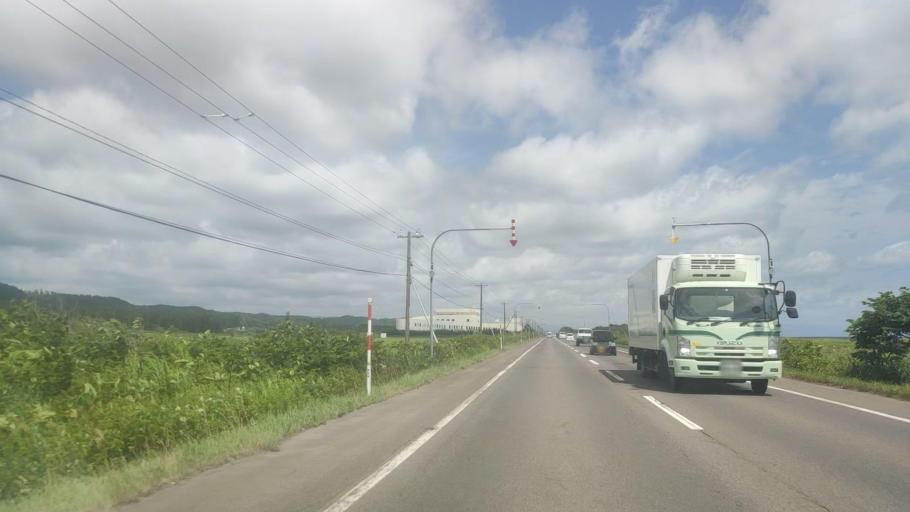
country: JP
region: Hokkaido
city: Niseko Town
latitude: 42.3825
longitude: 140.2943
